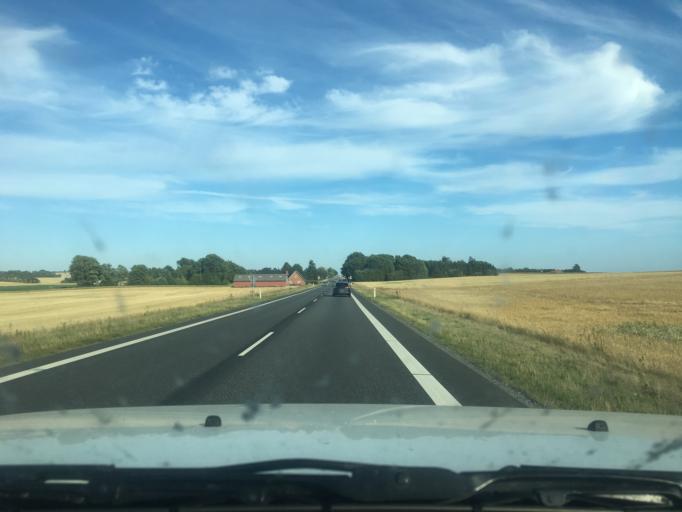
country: DK
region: Central Jutland
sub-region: Syddjurs Kommune
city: Hornslet
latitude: 56.3862
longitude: 10.2840
